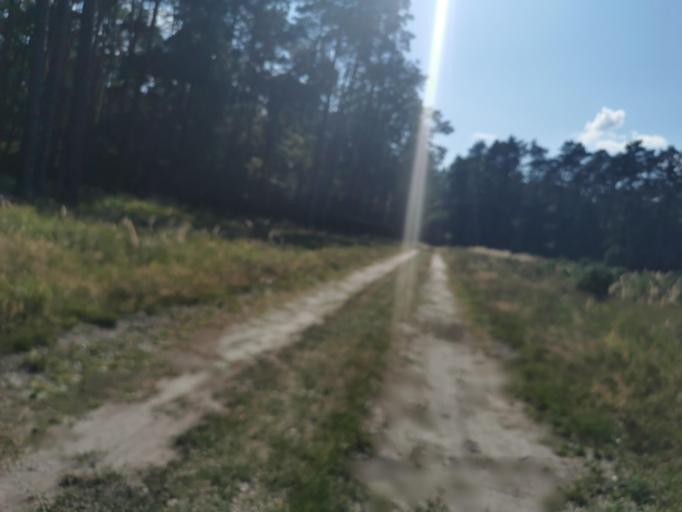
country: SK
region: Trnavsky
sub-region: Okres Senica
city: Senica
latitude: 48.6078
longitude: 17.2716
